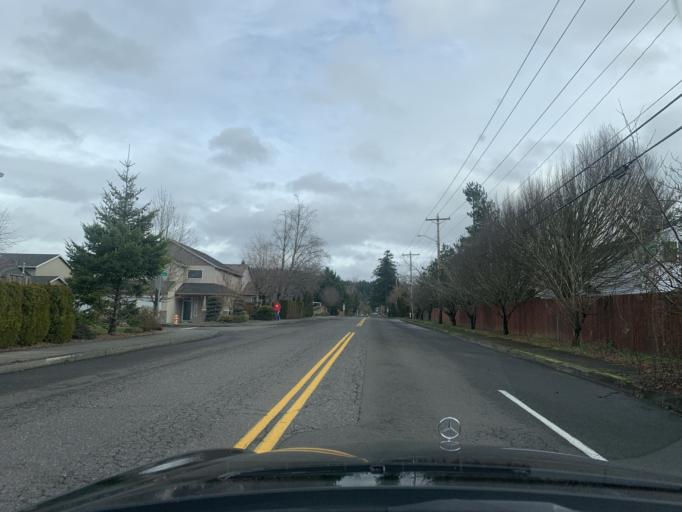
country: US
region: Oregon
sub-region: Multnomah County
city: Gresham
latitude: 45.4719
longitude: -122.4635
